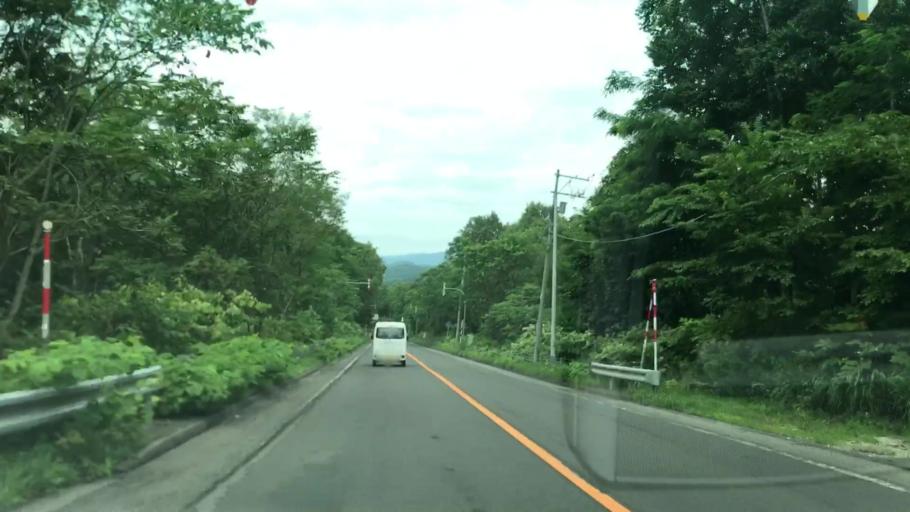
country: JP
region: Hokkaido
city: Niseko Town
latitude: 42.9456
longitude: 140.7048
